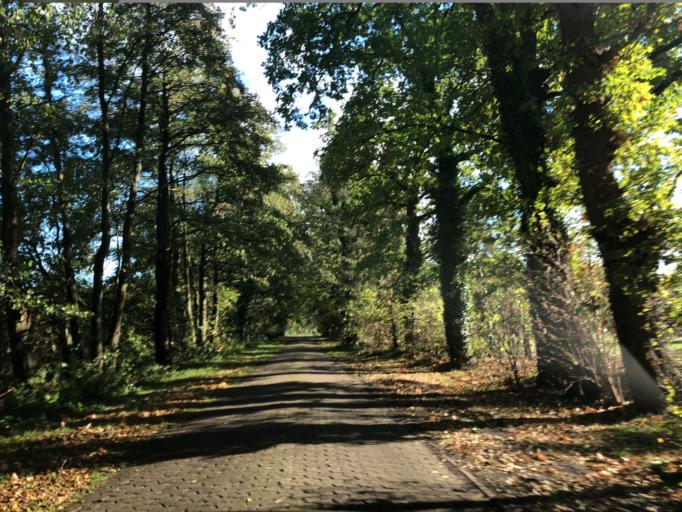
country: DE
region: Lower Saxony
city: Lehe
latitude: 53.0357
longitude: 7.3439
